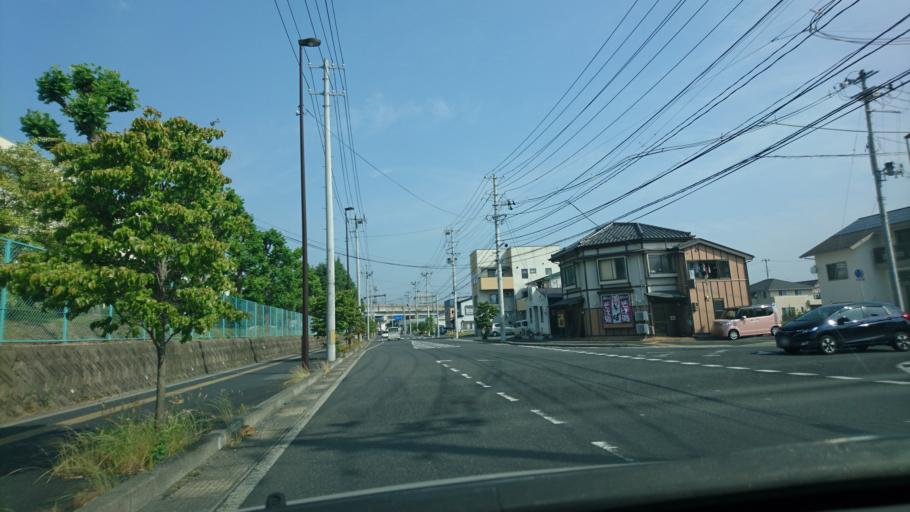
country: JP
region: Iwate
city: Ichinoseki
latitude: 38.9264
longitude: 141.1424
